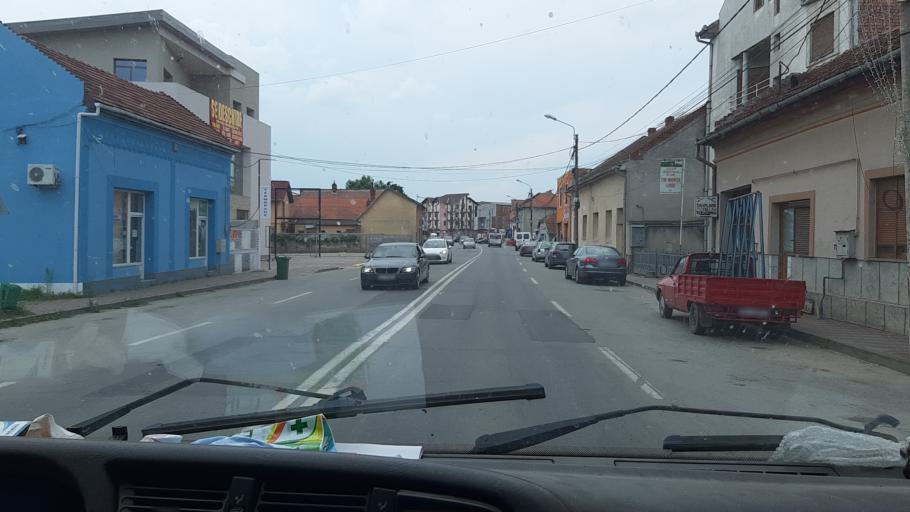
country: RO
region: Timis
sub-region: Municipiul Lugoj
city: Lugoj
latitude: 45.6929
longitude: 21.9021
